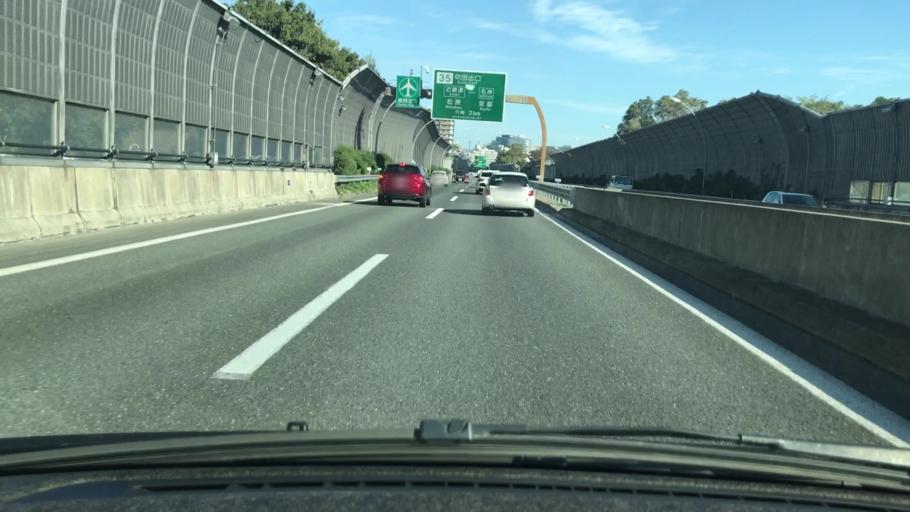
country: JP
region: Osaka
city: Suita
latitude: 34.7859
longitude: 135.5298
